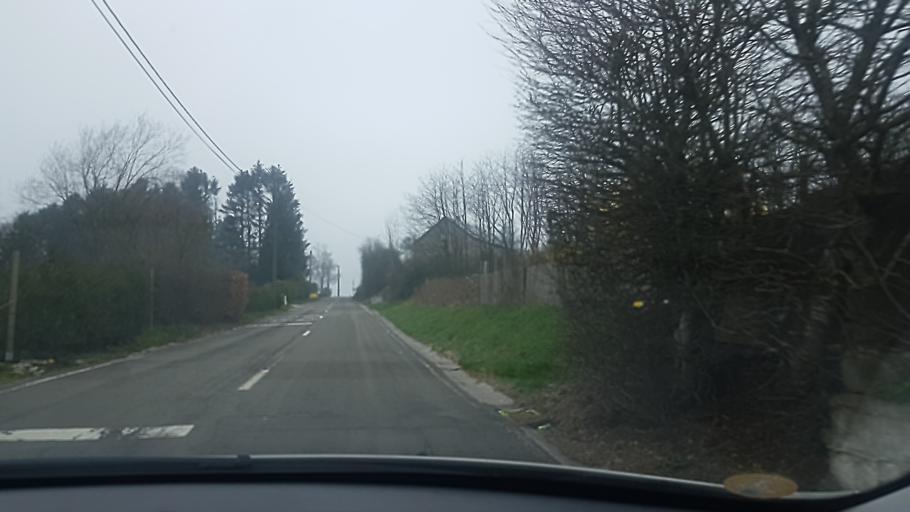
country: FR
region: Champagne-Ardenne
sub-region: Departement des Ardennes
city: Haybes
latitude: 50.0247
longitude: 4.6351
